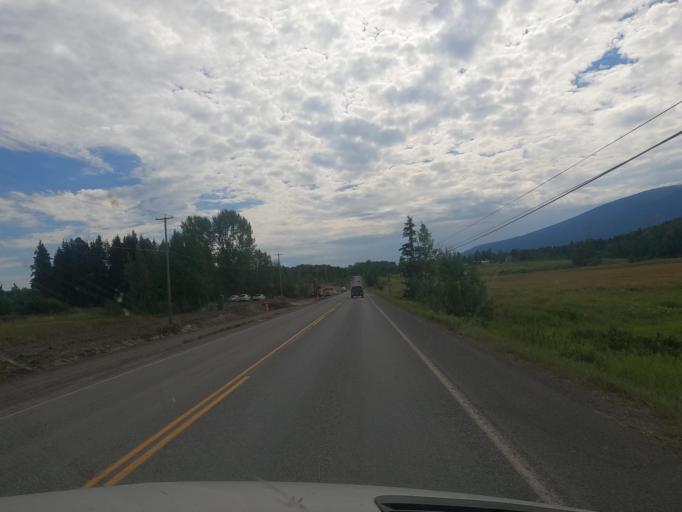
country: CA
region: British Columbia
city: Smithers
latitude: 54.8608
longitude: -127.2288
